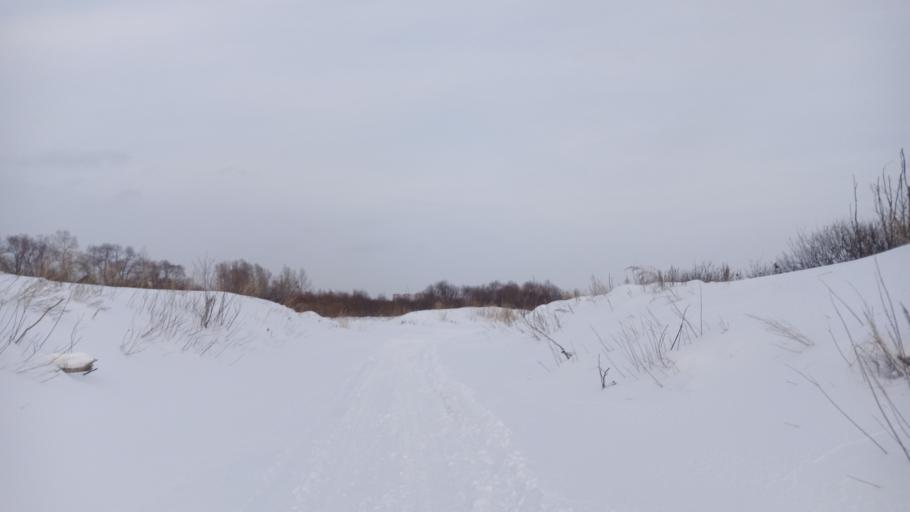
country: RU
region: Altai Krai
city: Yuzhnyy
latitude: 53.3078
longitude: 83.7207
